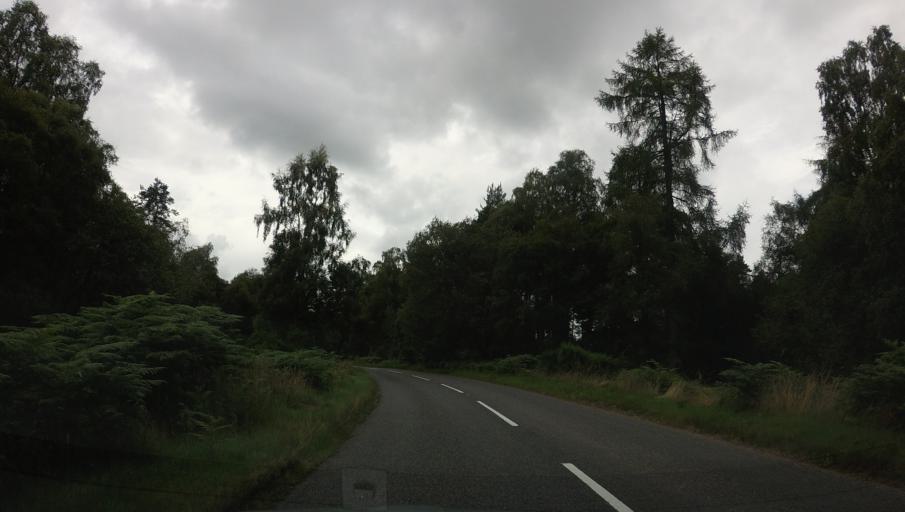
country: GB
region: Scotland
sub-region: Aberdeenshire
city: Torphins
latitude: 57.0650
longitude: -2.6808
